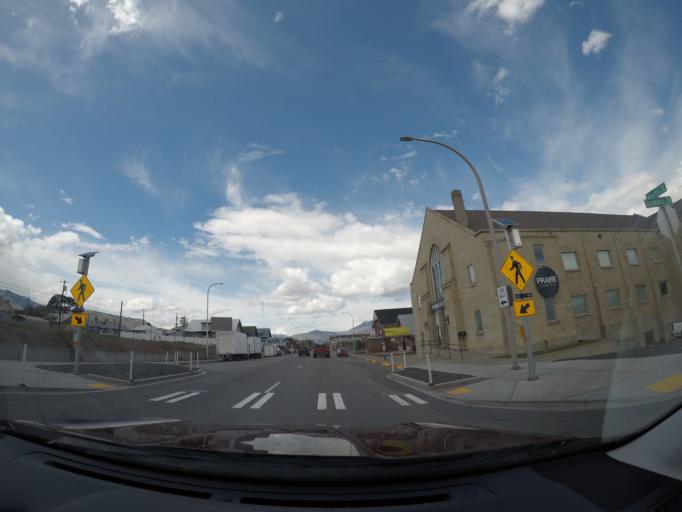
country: US
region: Washington
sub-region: Chelan County
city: Wenatchee
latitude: 47.4180
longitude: -120.3076
